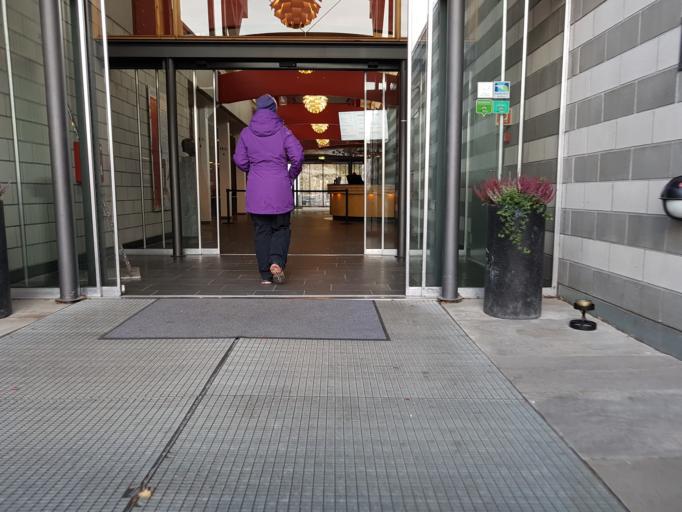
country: NO
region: Oppland
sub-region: Lillehammer
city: Lillehammer
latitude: 61.1119
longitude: 10.4773
